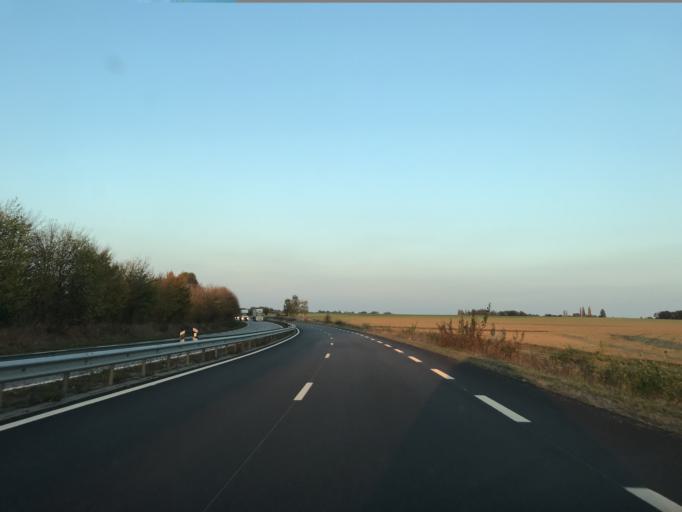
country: FR
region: Haute-Normandie
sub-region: Departement de l'Eure
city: Bourth
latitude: 48.6662
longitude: 0.7821
